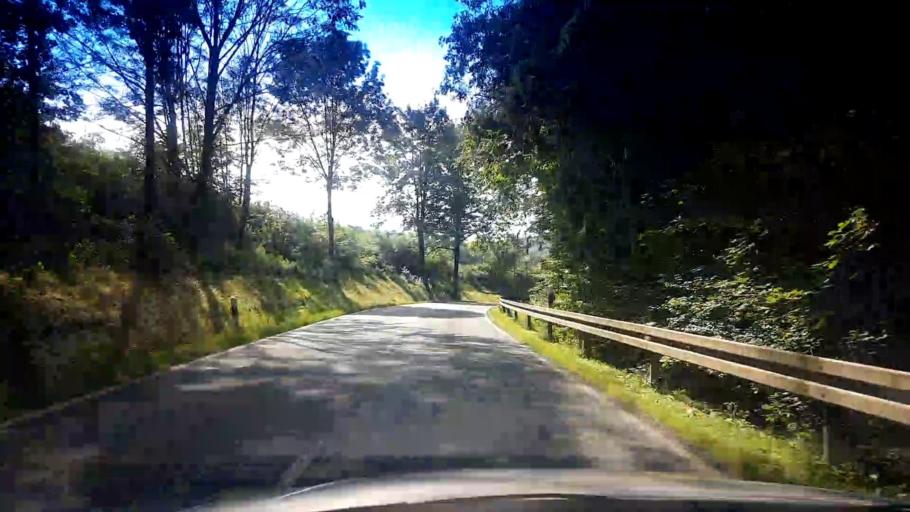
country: DE
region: Bavaria
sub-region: Upper Franconia
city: Hollfeld
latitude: 49.9381
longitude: 11.3429
